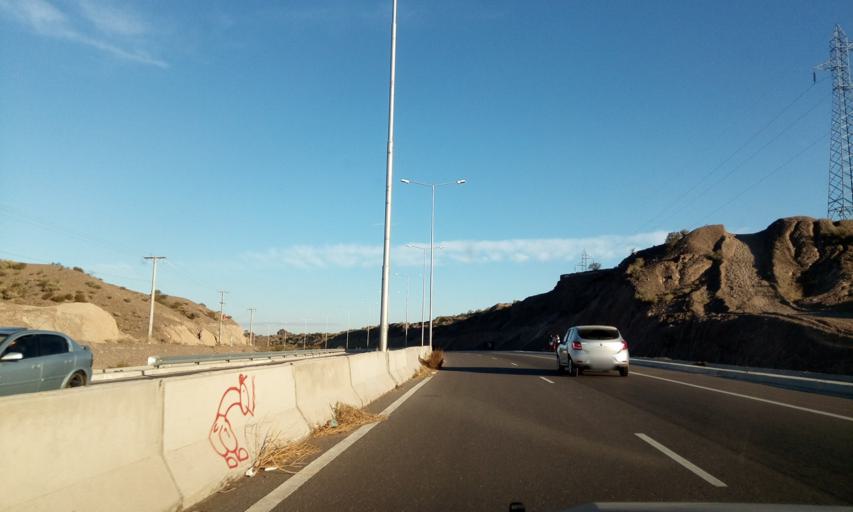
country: AR
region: San Juan
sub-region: Departamento de Rivadavia
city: Rivadavia
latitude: -31.4994
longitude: -68.6490
